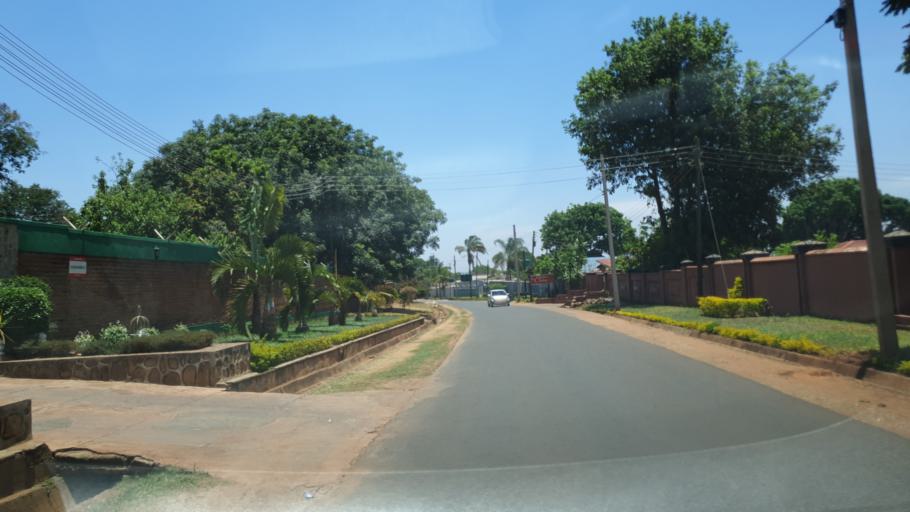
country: MW
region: Central Region
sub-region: Lilongwe District
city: Lilongwe
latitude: -13.9792
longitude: 33.7458
